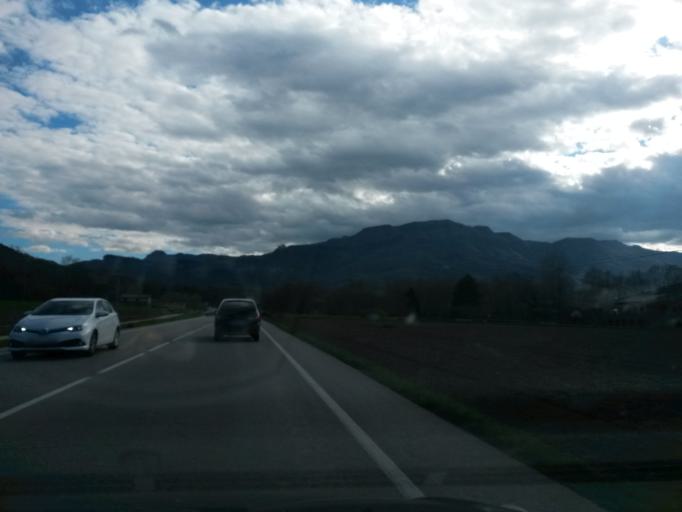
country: ES
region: Catalonia
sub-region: Provincia de Girona
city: Bas
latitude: 42.1333
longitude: 2.4524
